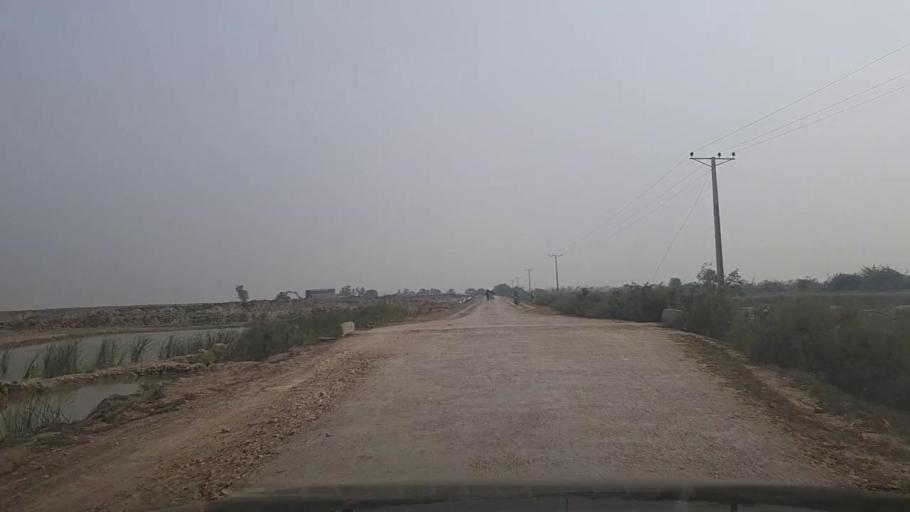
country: PK
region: Sindh
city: Mirpur Sakro
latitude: 24.4752
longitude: 67.6661
